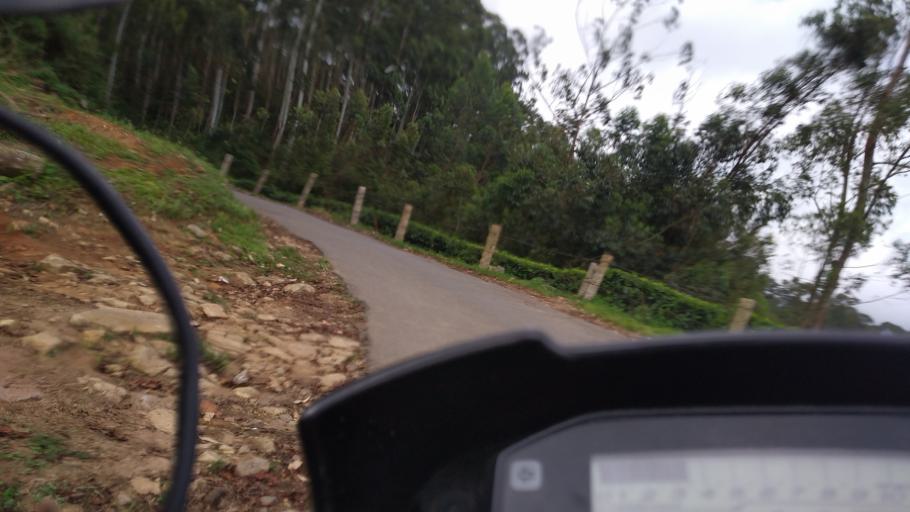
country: IN
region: Kerala
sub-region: Idukki
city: Munnar
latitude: 10.0354
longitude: 77.1703
